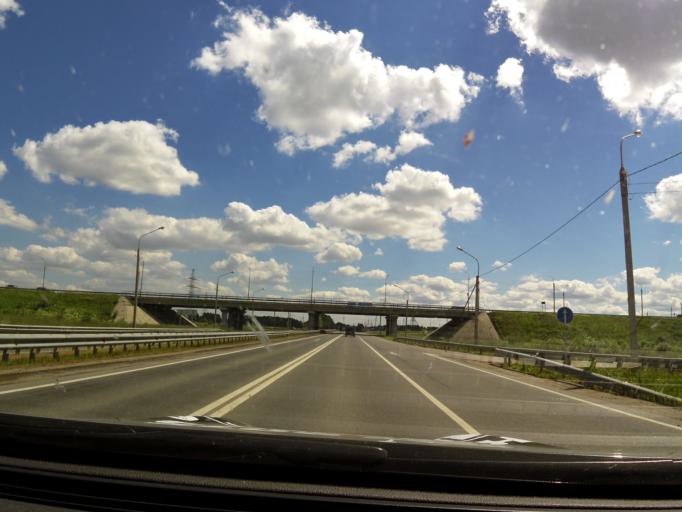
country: RU
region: Vologda
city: Molochnoye
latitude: 59.2486
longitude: 39.7735
